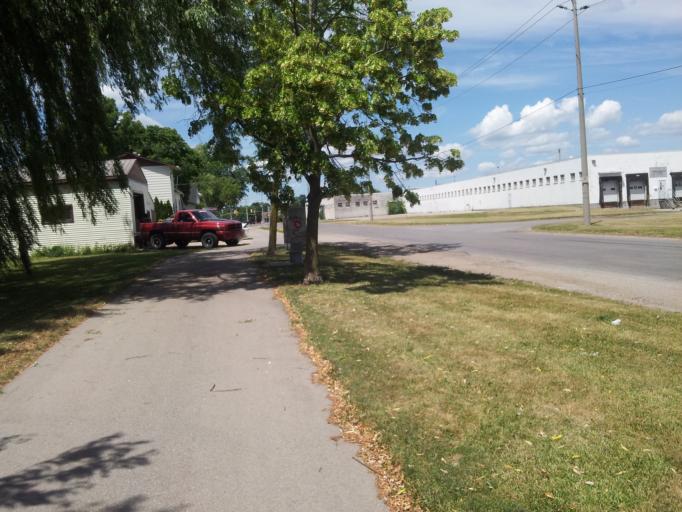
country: CA
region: Ontario
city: Stratford
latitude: 43.3686
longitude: -80.9579
